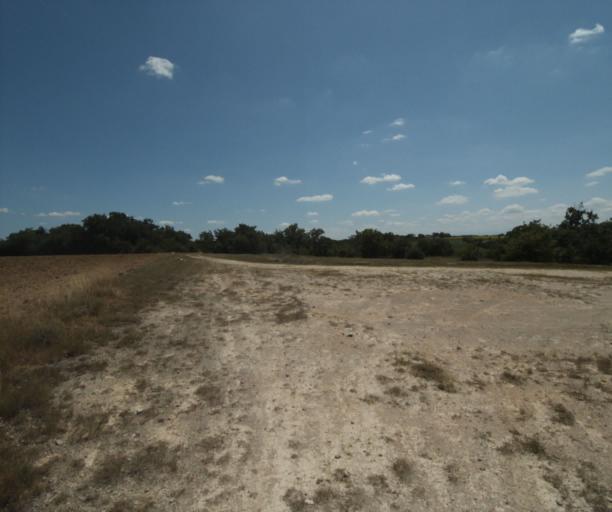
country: FR
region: Midi-Pyrenees
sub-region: Departement de la Haute-Garonne
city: Auriac-sur-Vendinelle
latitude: 43.4878
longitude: 1.8527
